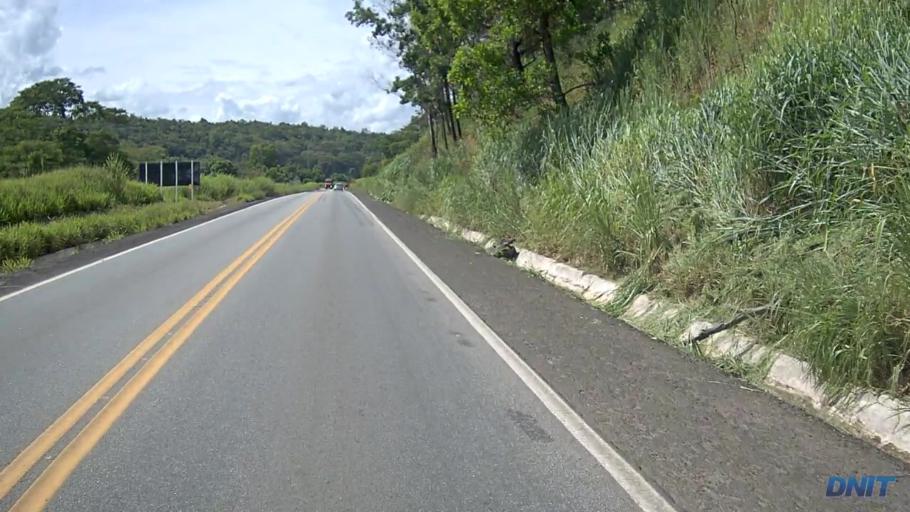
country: BR
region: Minas Gerais
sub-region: Ipaba
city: Ipaba
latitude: -19.3994
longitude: -42.4837
